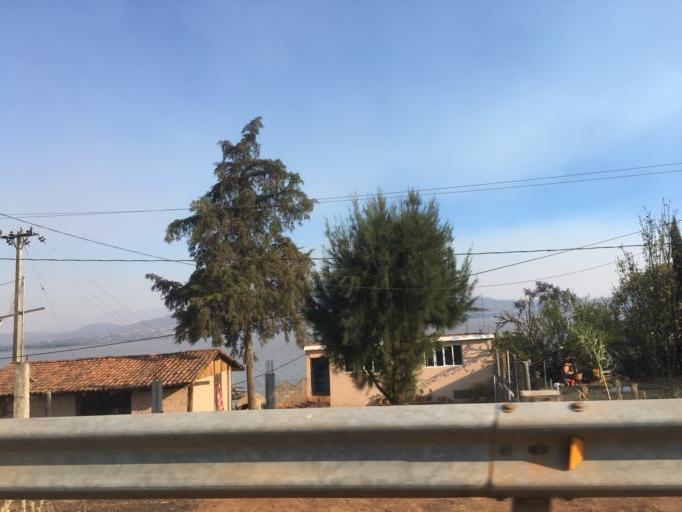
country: MX
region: Michoacan
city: Santa Fe de la Laguna
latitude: 19.6700
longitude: -101.5667
